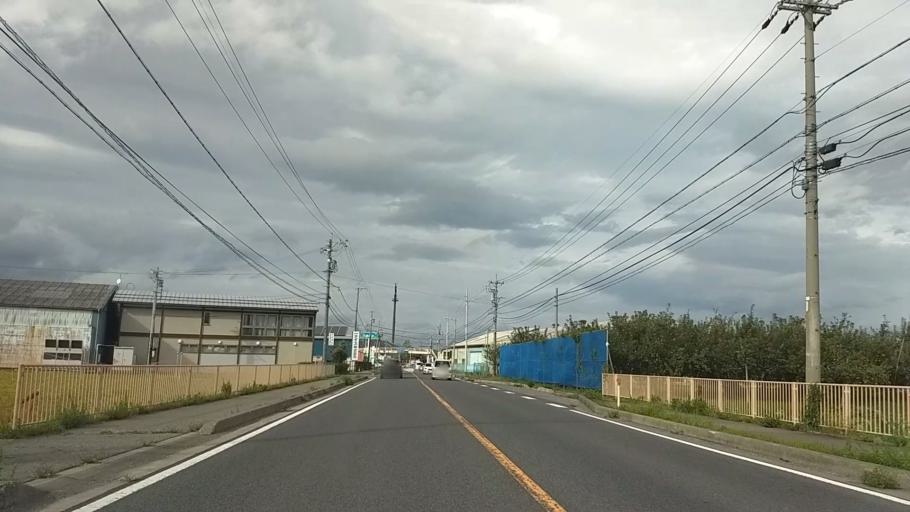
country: JP
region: Nagano
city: Suzaka
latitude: 36.6733
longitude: 138.2664
